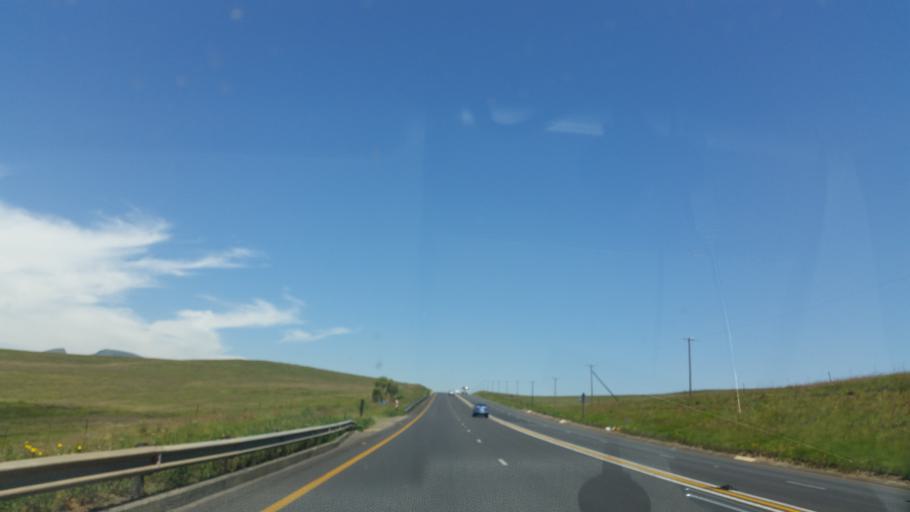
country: ZA
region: Orange Free State
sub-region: Thabo Mofutsanyana District Municipality
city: Harrismith
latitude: -28.3665
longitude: 29.3526
